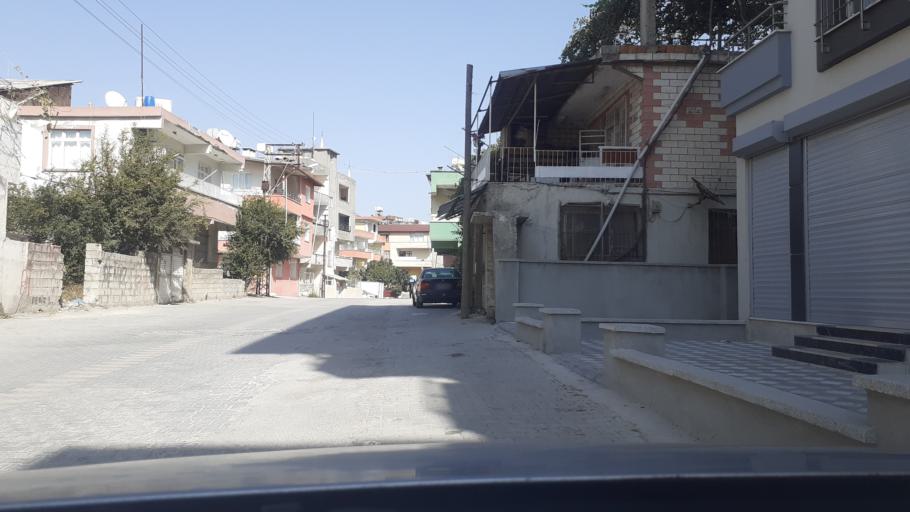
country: TR
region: Hatay
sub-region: Antakya Ilcesi
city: Antakya
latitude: 36.2109
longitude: 36.1513
